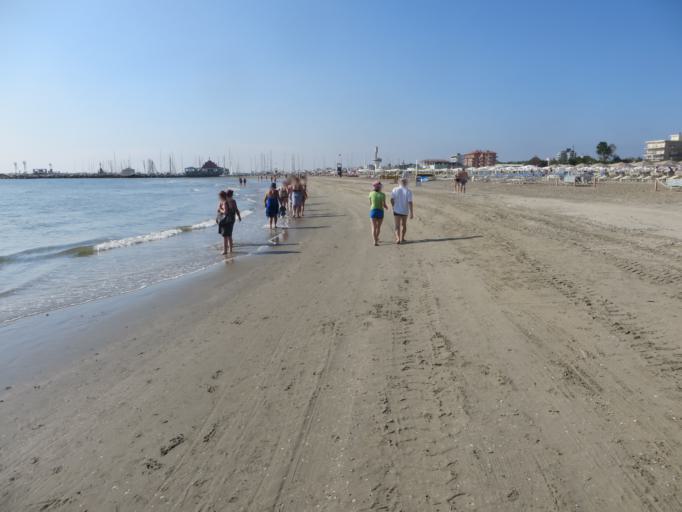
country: IT
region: Emilia-Romagna
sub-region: Provincia di Ravenna
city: Cervia
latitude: 44.2712
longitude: 12.3573
